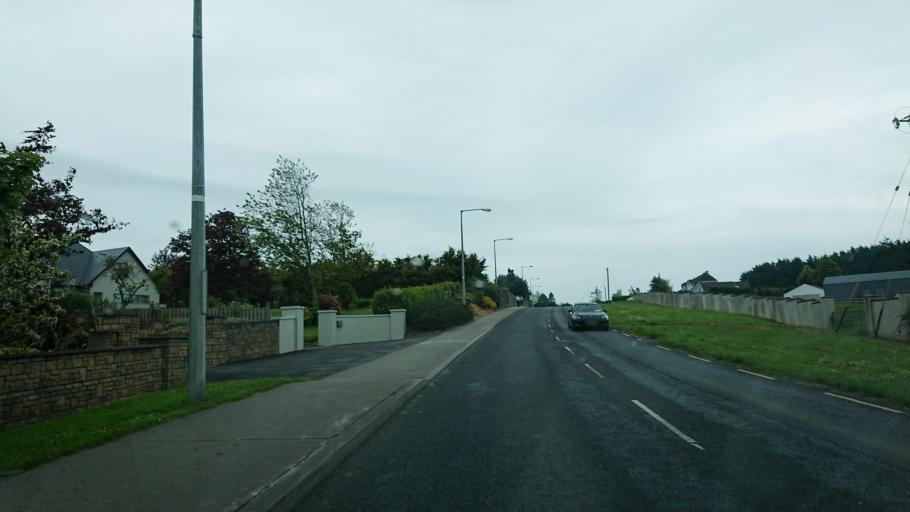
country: IE
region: Munster
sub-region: Waterford
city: Waterford
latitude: 52.2381
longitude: -7.0835
